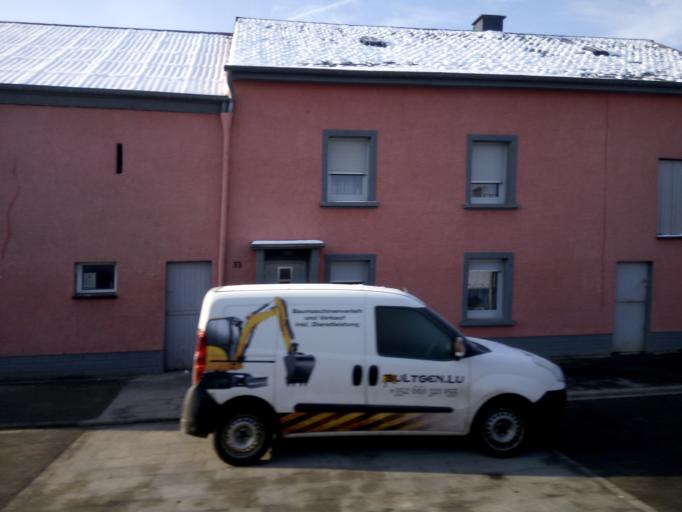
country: LU
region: Grevenmacher
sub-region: Canton d'Echternach
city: Consdorf
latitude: 49.7877
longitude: 6.3461
